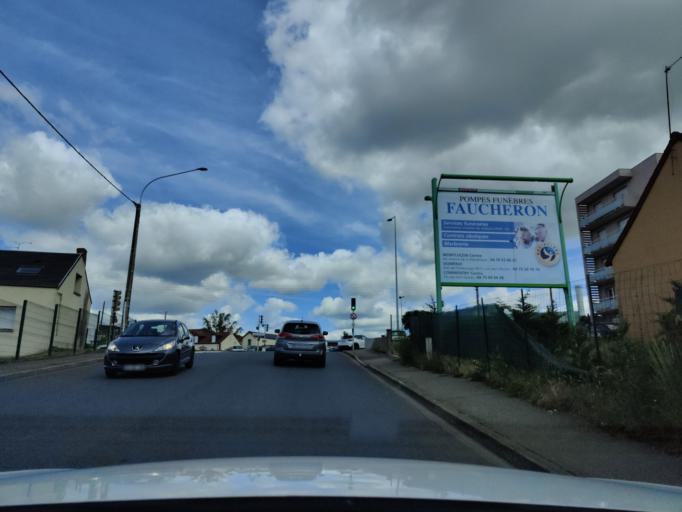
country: FR
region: Auvergne
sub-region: Departement de l'Allier
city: Montlucon
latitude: 46.3430
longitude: 2.6111
